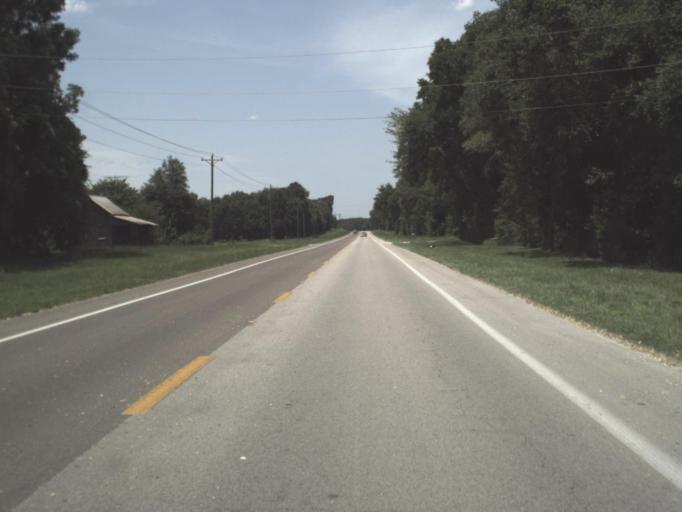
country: US
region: Florida
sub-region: Gilchrist County
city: Trenton
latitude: 29.7308
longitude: -82.8578
